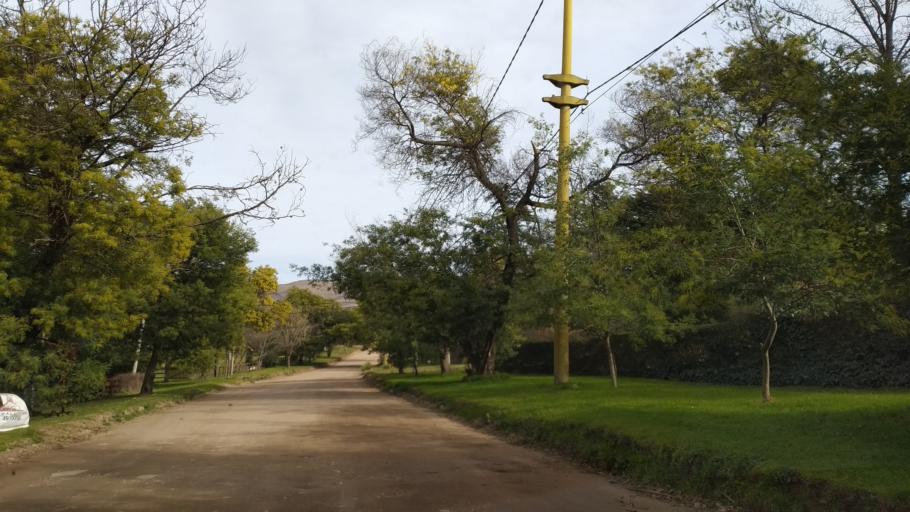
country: AR
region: Buenos Aires
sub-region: Partido de Tornquist
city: Tornquist
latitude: -38.0850
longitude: -61.9298
